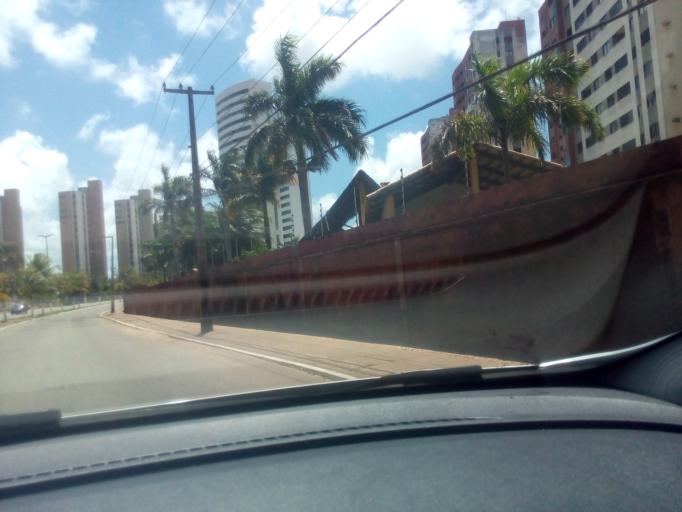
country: BR
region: Rio Grande do Norte
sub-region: Parnamirim
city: Parnamirim
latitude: -5.8924
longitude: -35.1930
